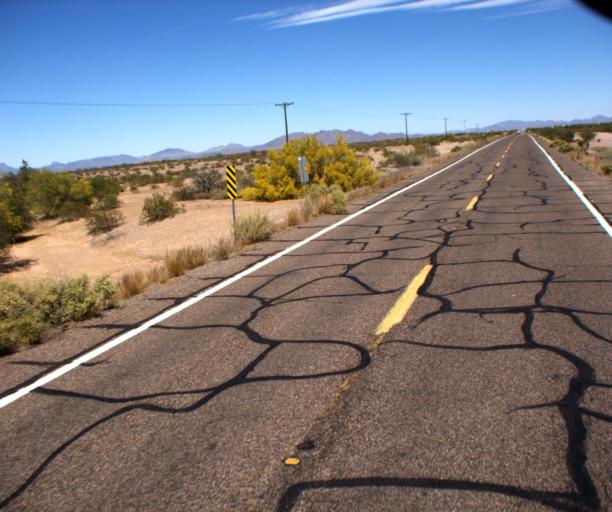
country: US
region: Arizona
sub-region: Maricopa County
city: Gila Bend
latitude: 32.8879
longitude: -112.7501
